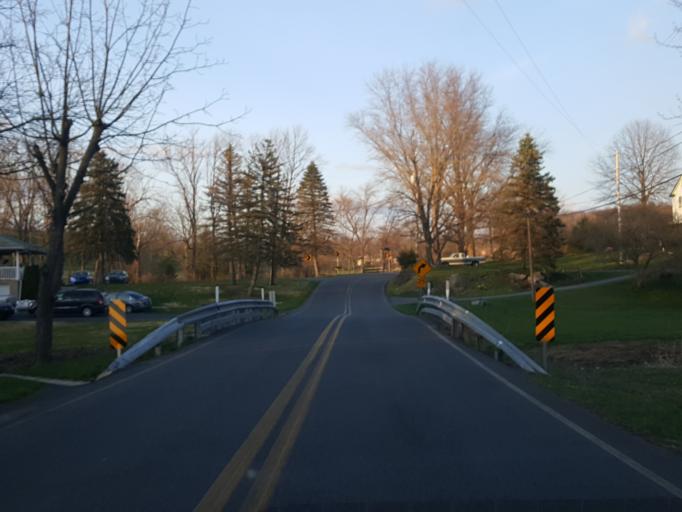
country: US
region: Pennsylvania
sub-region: Lebanon County
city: Jonestown
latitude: 40.3984
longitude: -76.4829
